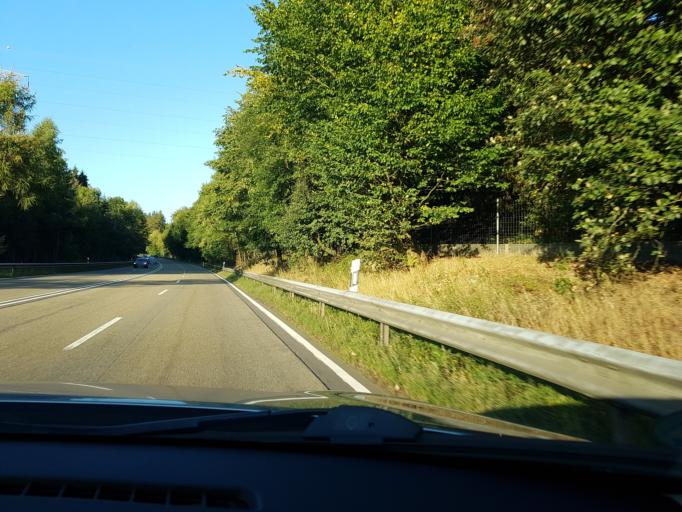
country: DE
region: Rheinland-Pfalz
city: Fachbach
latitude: 50.3506
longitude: 7.6751
